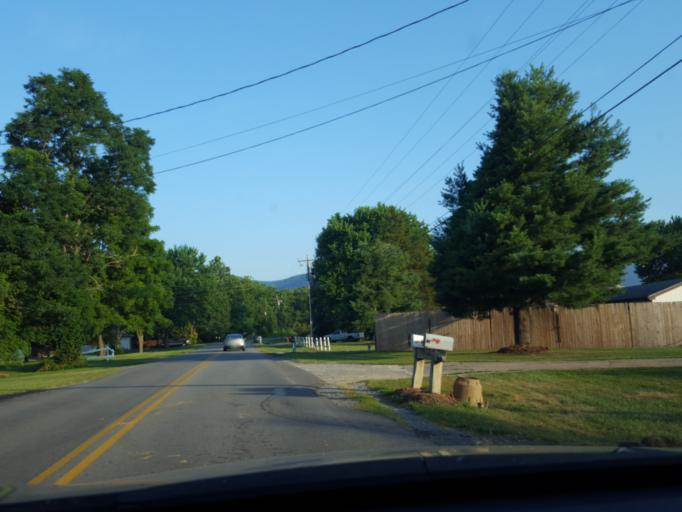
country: US
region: Virginia
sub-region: Augusta County
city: Lyndhurst
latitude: 37.9851
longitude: -78.9551
